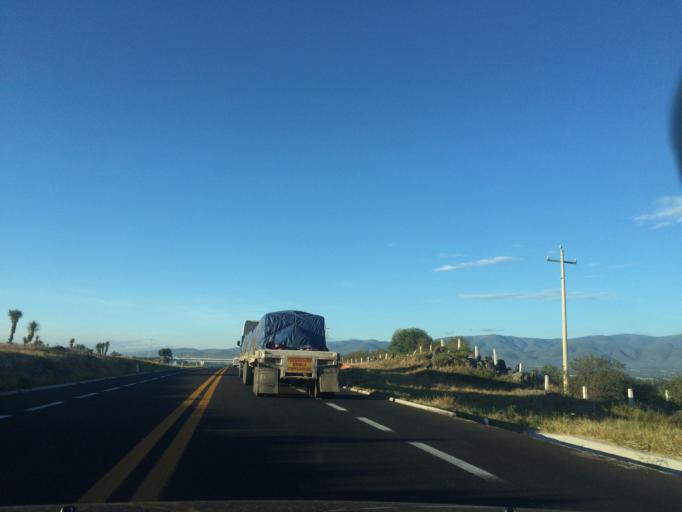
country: MX
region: Puebla
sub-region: Tehuacan
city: Magdalena Cuayucatepec
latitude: 18.5534
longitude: -97.4630
